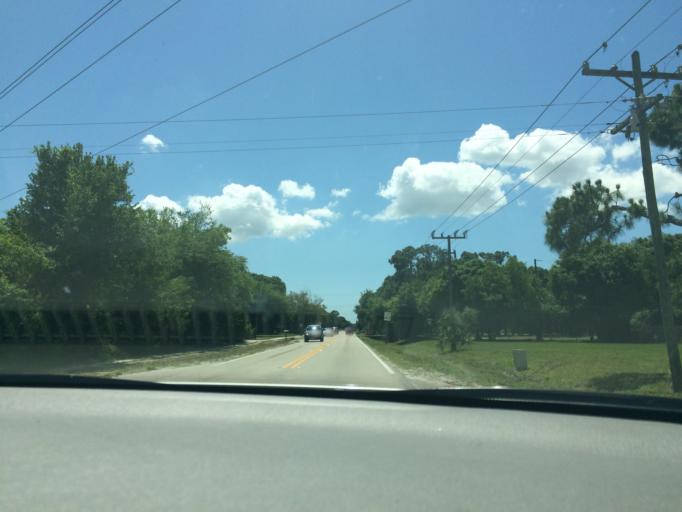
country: US
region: Florida
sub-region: Manatee County
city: Samoset
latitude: 27.4832
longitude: -82.4895
